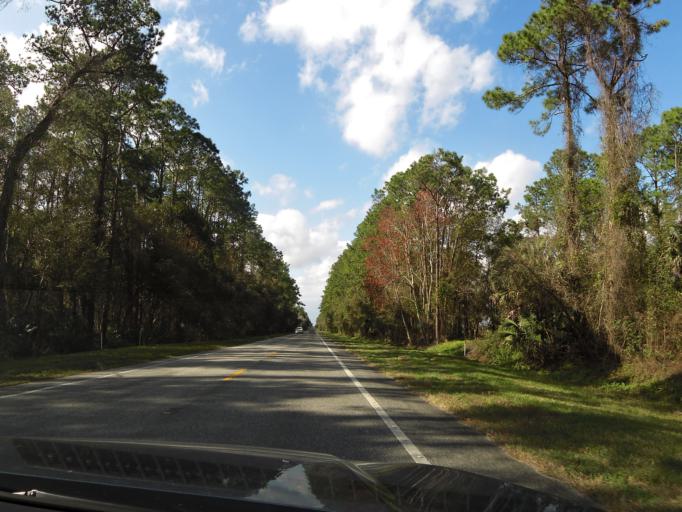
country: US
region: Florida
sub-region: Volusia County
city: De Leon Springs
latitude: 29.1460
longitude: -81.3684
